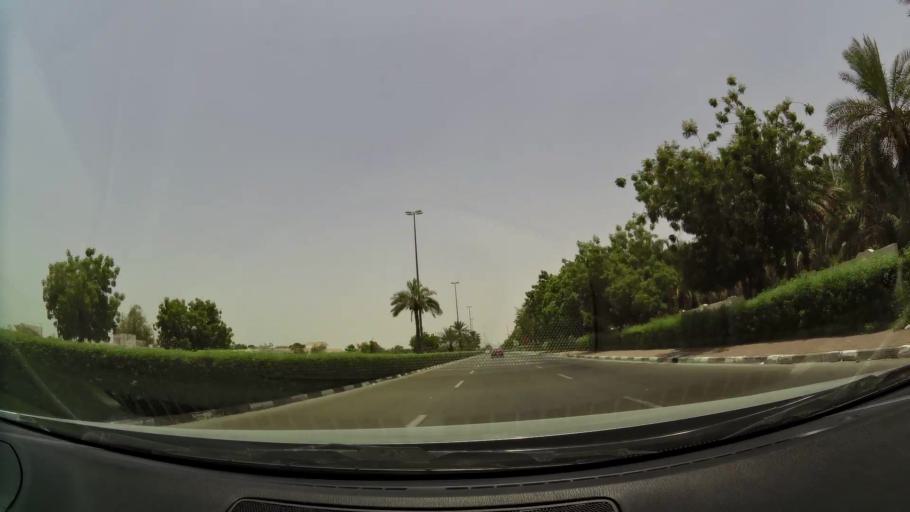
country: AE
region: Abu Dhabi
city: Al Ain
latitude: 24.2235
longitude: 55.7320
